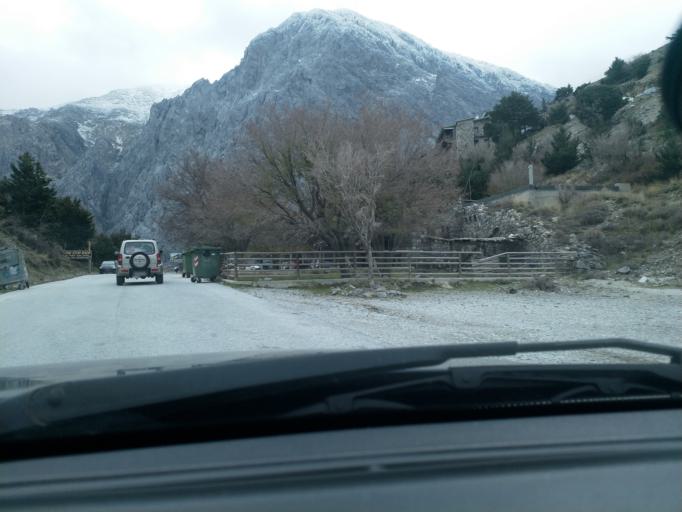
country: GR
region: Crete
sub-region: Nomos Chanias
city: Perivolia
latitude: 35.3089
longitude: 23.9180
